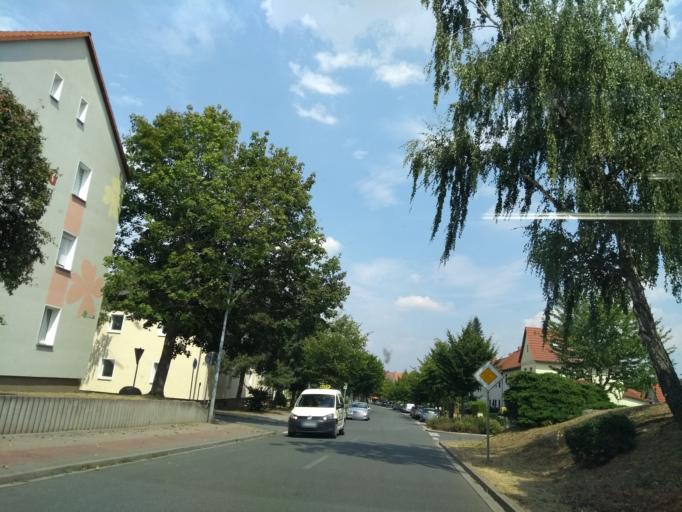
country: DE
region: Saxony-Anhalt
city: Zeitz
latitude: 51.0423
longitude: 12.1200
